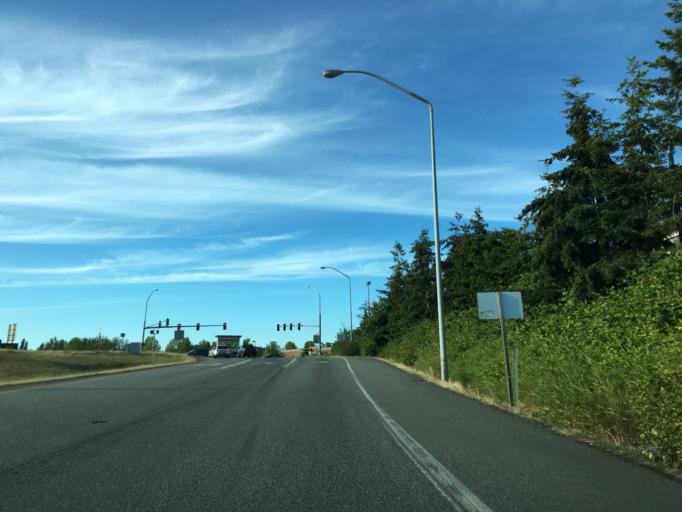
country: US
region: Washington
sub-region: Whatcom County
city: Bellingham
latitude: 48.7703
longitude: -122.4626
